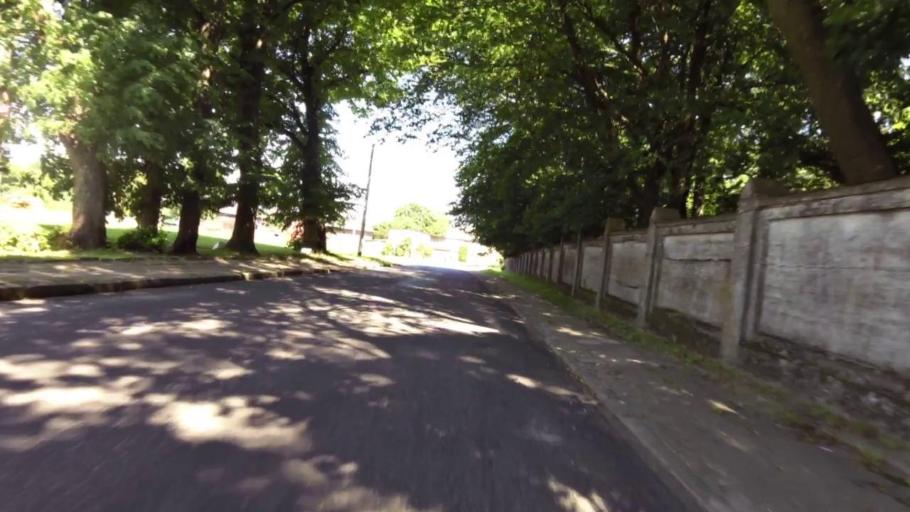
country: PL
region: West Pomeranian Voivodeship
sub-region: Powiat swidwinski
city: Rabino
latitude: 53.8437
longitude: 15.9980
